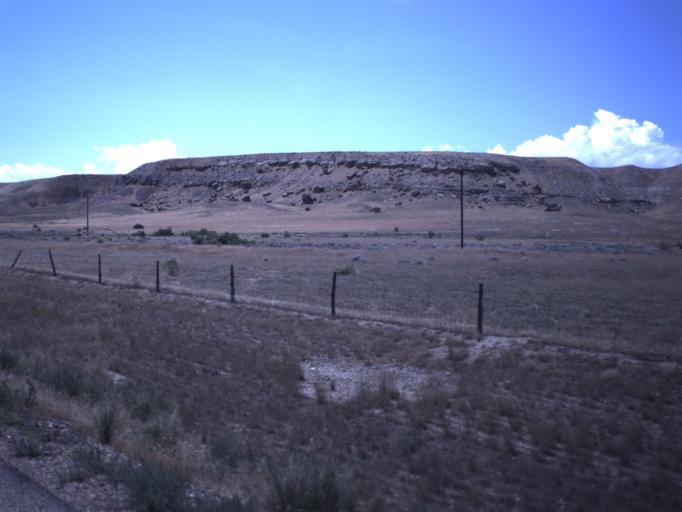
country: US
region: Utah
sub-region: Uintah County
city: Naples
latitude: 40.1124
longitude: -109.6689
